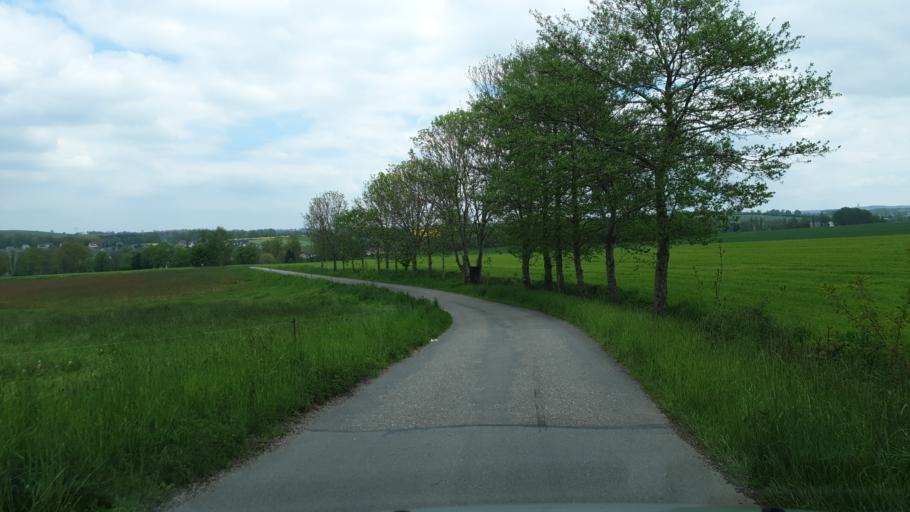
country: DE
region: Saxony
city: Hohndorf
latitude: 50.7657
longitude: 12.6938
